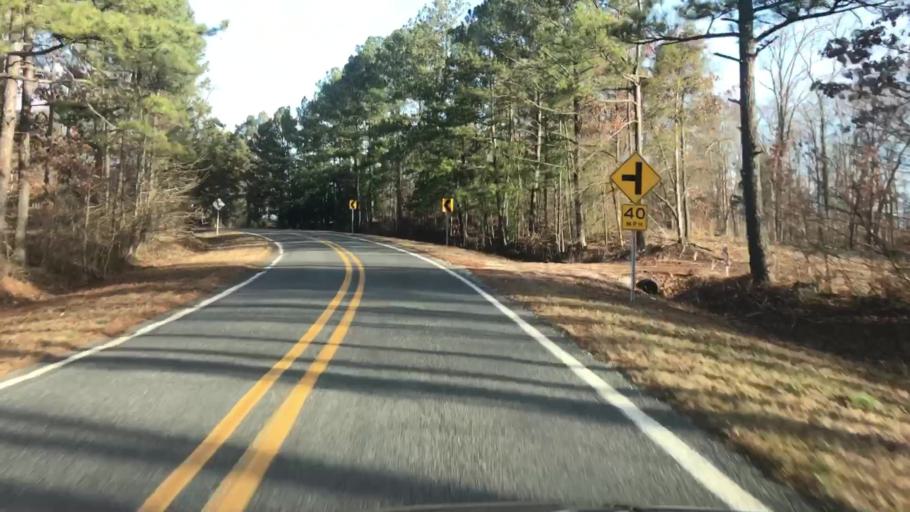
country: US
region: Arkansas
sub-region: Garland County
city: Rockwell
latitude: 34.4921
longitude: -93.2757
